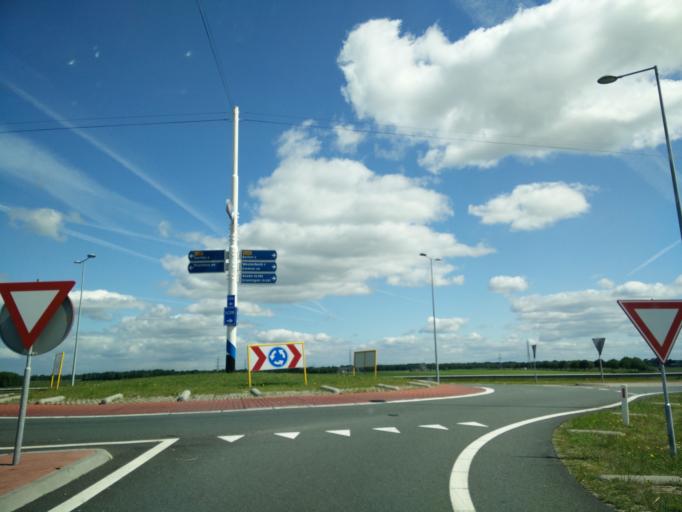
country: NL
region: Drenthe
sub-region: Gemeente Assen
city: Assen
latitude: 52.8781
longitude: 6.5100
